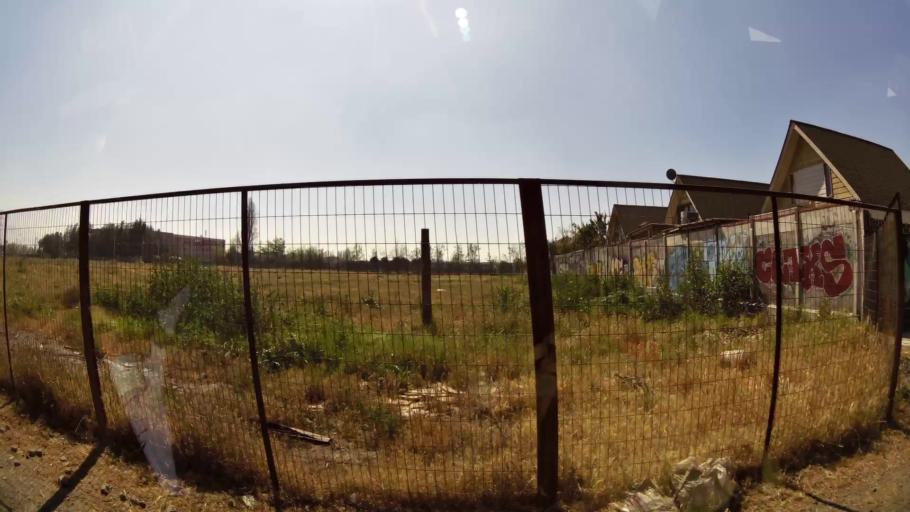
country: CL
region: Santiago Metropolitan
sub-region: Provincia de Santiago
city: Lo Prado
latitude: -33.3585
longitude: -70.7246
